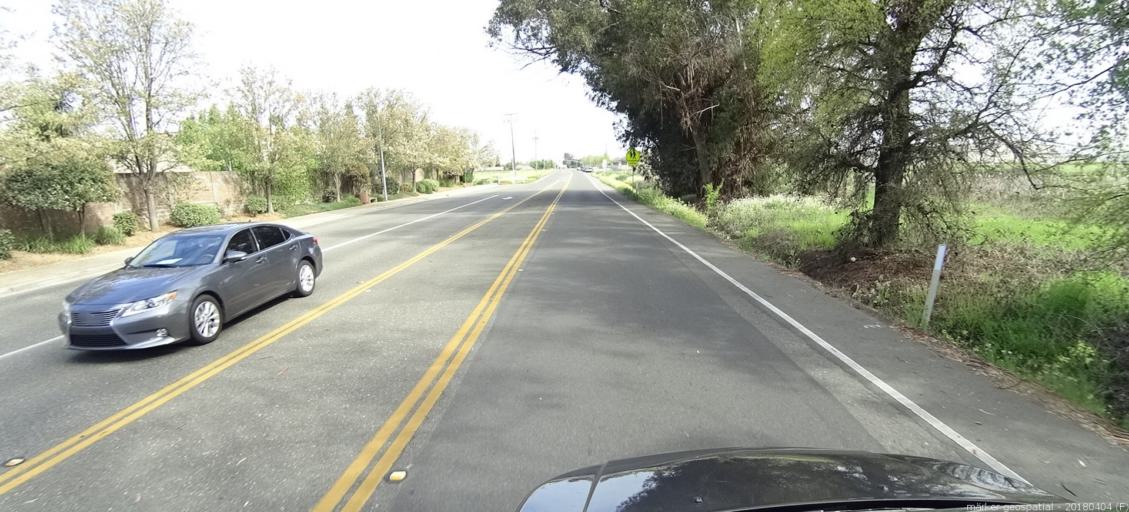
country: US
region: California
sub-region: Sacramento County
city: Galt
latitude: 38.2833
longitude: -121.2826
